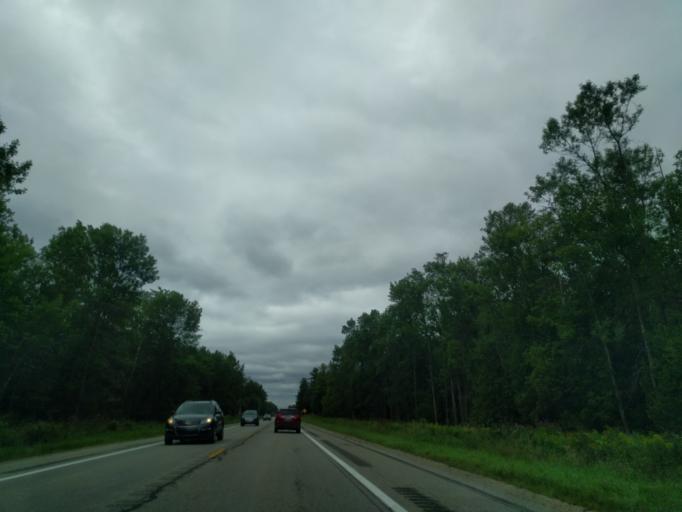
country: US
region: Michigan
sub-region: Delta County
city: Escanaba
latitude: 45.5817
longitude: -87.2430
